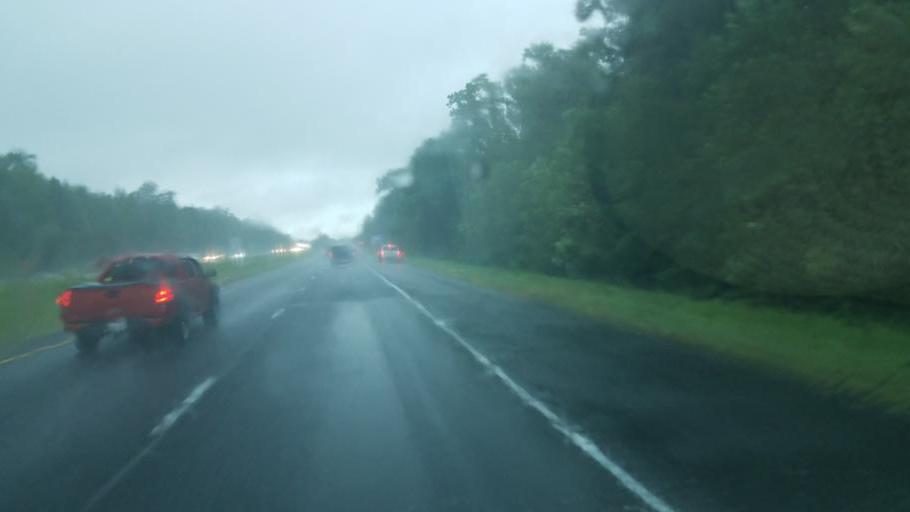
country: US
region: Virginia
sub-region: City of Portsmouth
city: Portsmouth Heights
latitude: 36.8316
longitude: -76.4333
